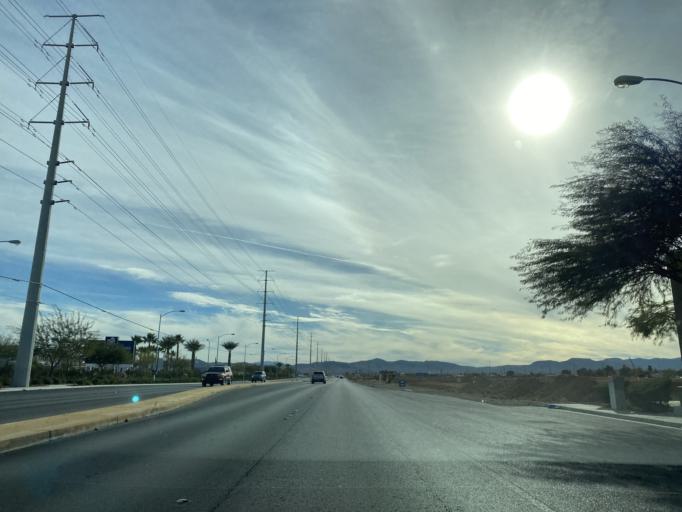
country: US
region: Nevada
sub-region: Clark County
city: Enterprise
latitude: 36.0316
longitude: -115.2436
